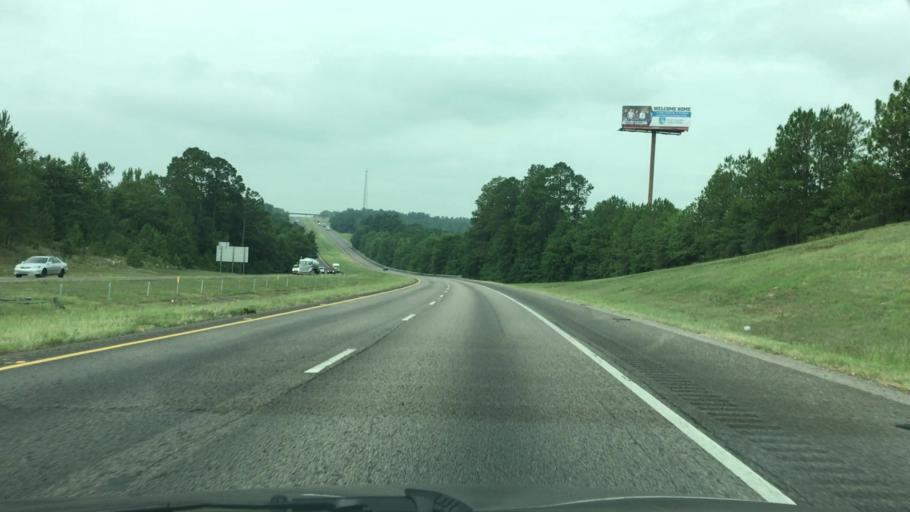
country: US
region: South Carolina
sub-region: Aiken County
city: Graniteville
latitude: 33.6003
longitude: -81.8660
